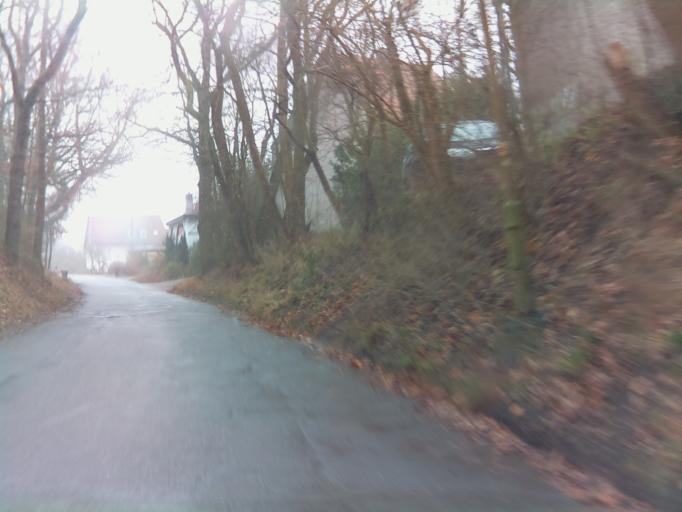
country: DE
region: Thuringia
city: Stadtroda
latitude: 50.8534
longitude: 11.7355
